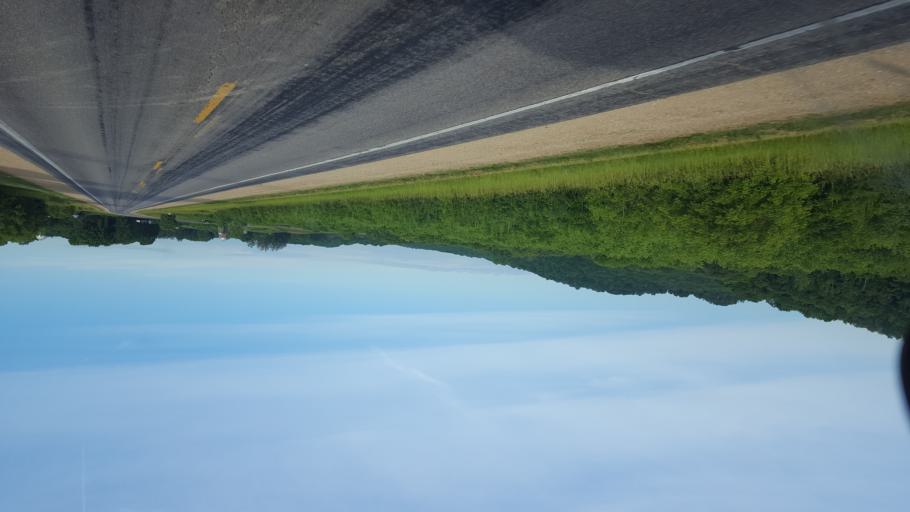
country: US
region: Wisconsin
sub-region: Vernon County
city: Hillsboro
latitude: 43.6585
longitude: -90.3702
